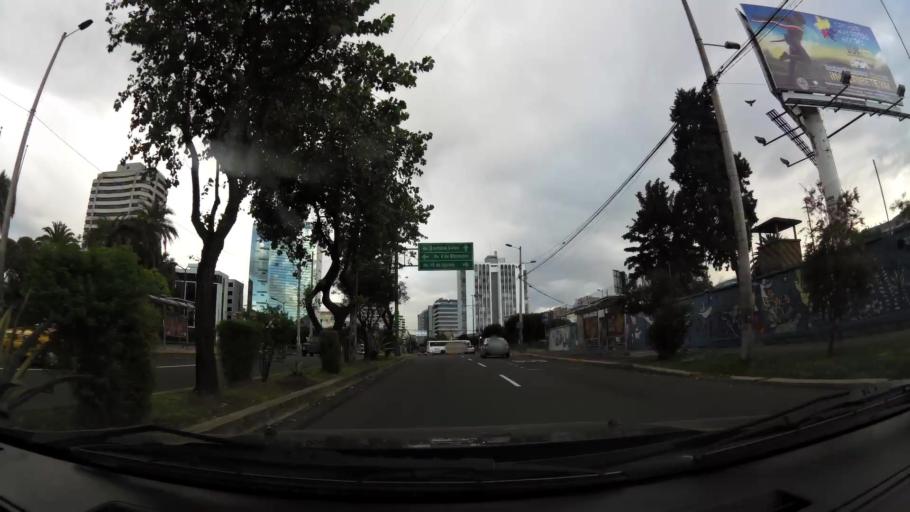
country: EC
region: Pichincha
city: Quito
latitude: -0.1964
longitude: -78.4893
